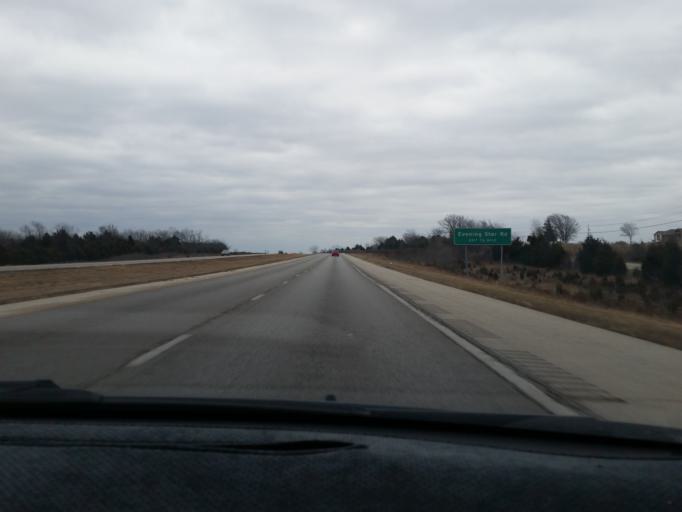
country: US
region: Kansas
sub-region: Douglas County
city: Eudora
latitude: 38.9429
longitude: -95.0520
